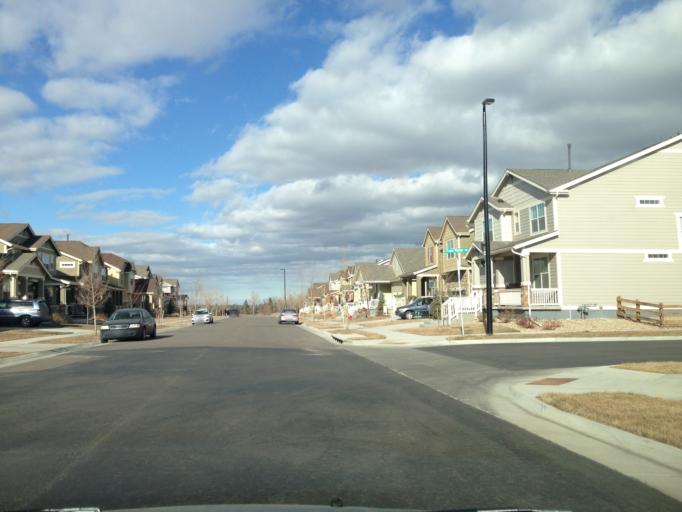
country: US
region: Colorado
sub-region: Boulder County
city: Lafayette
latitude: 40.0317
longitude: -105.0897
